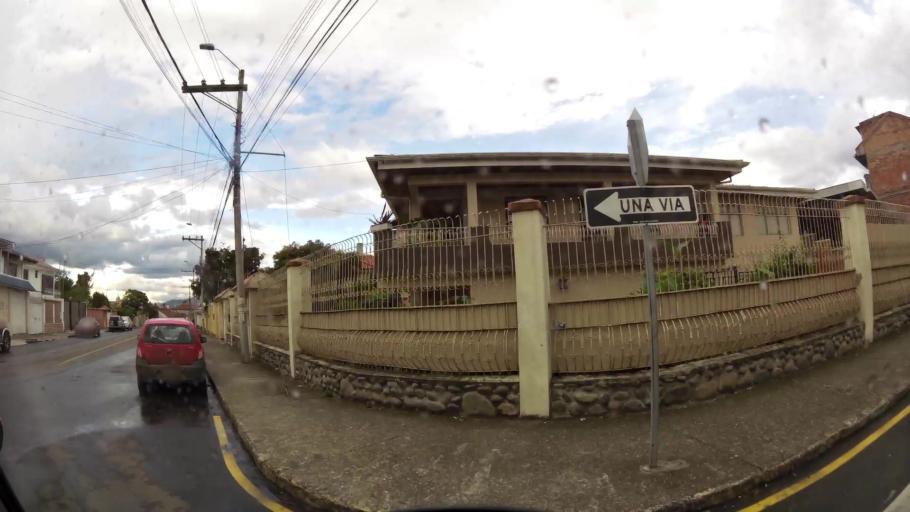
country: EC
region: Azuay
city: Cuenca
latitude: -2.8970
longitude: -79.0185
